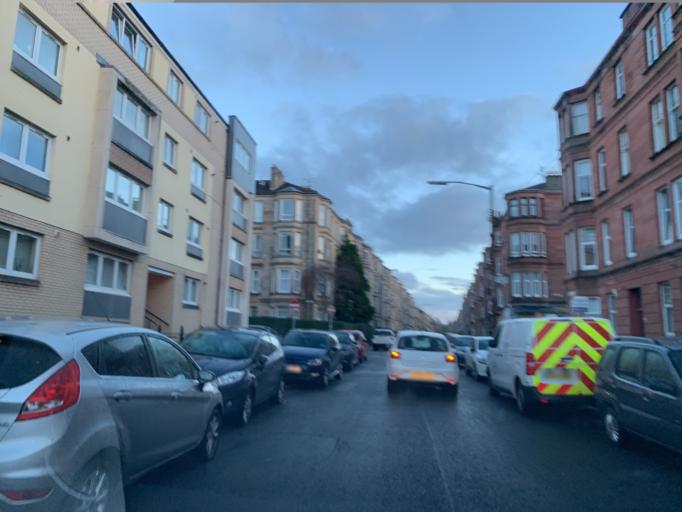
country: GB
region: Scotland
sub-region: East Renfrewshire
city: Giffnock
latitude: 55.8274
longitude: -4.2830
